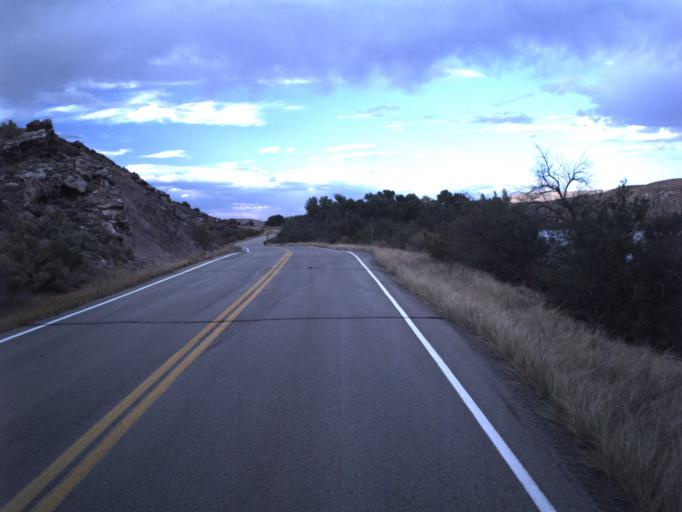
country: US
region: Utah
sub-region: Grand County
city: Moab
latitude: 38.8394
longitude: -109.2856
